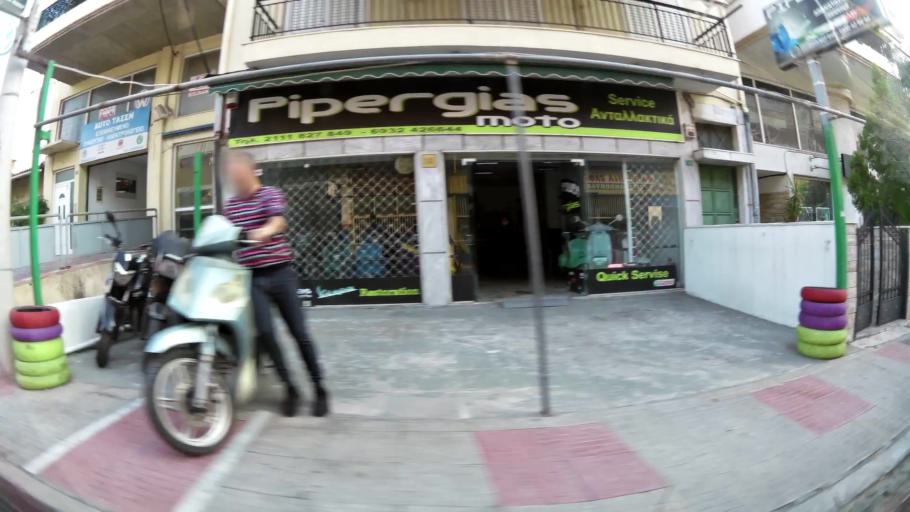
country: GR
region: Attica
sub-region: Nomarchia Athinas
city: Petroupolis
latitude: 38.0309
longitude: 23.6828
